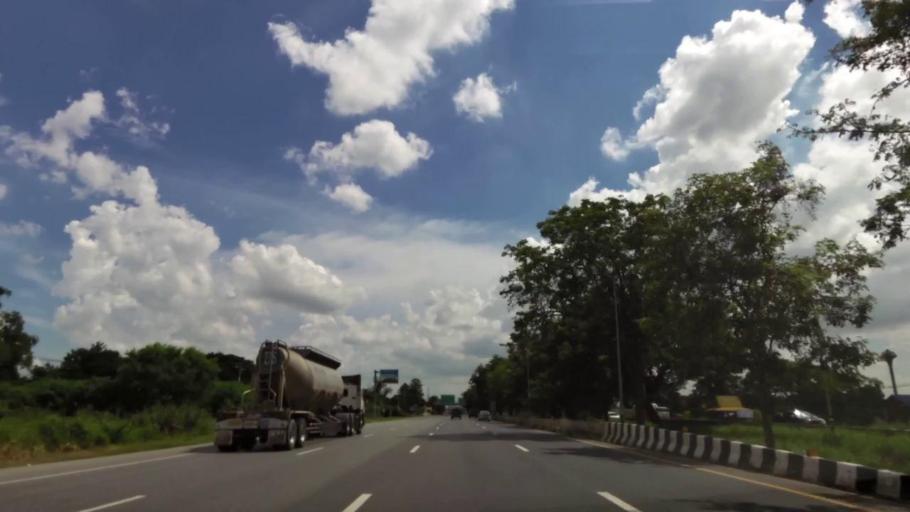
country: TH
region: Phra Nakhon Si Ayutthaya
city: Bang Pahan
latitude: 14.4685
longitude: 100.5362
